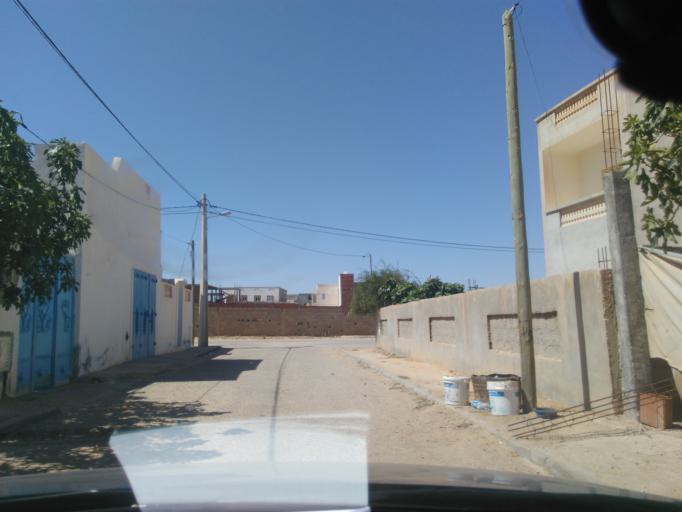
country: TN
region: Tataouine
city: Tataouine
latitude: 32.9503
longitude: 10.4696
